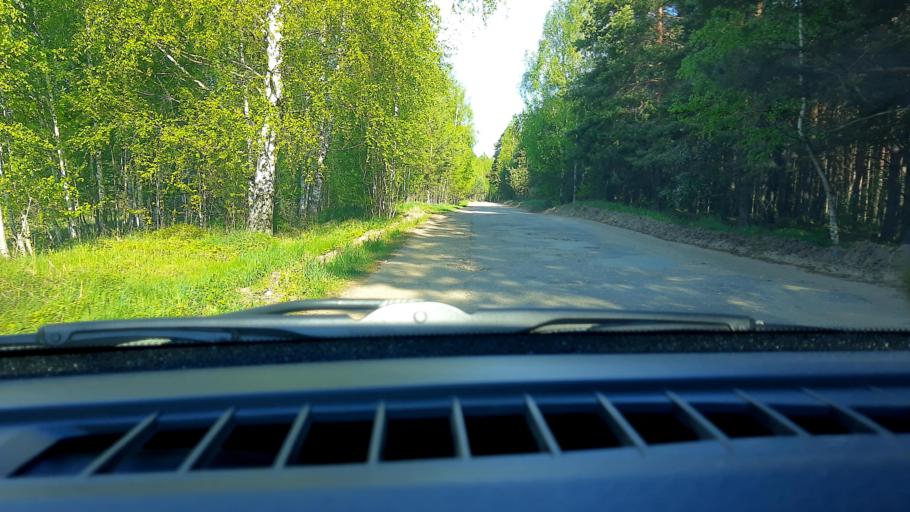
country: RU
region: Nizjnij Novgorod
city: Sitniki
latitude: 56.4137
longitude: 44.0564
